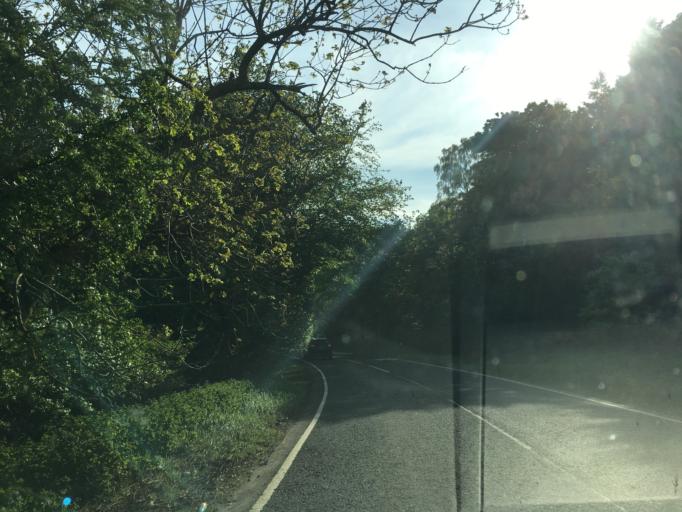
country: GB
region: Scotland
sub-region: The Scottish Borders
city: West Linton
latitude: 55.7031
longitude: -3.3608
